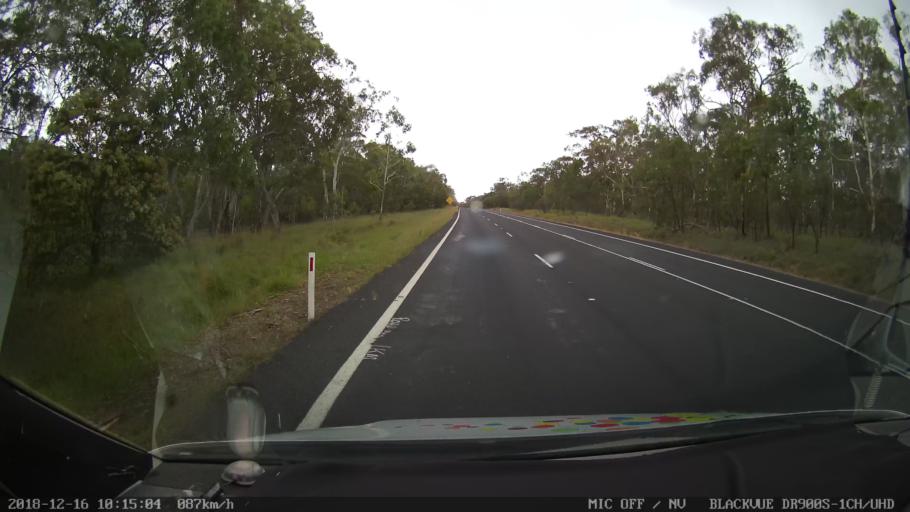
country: AU
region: New South Wales
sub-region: Tenterfield Municipality
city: Carrolls Creek
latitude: -29.2807
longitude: 151.9692
